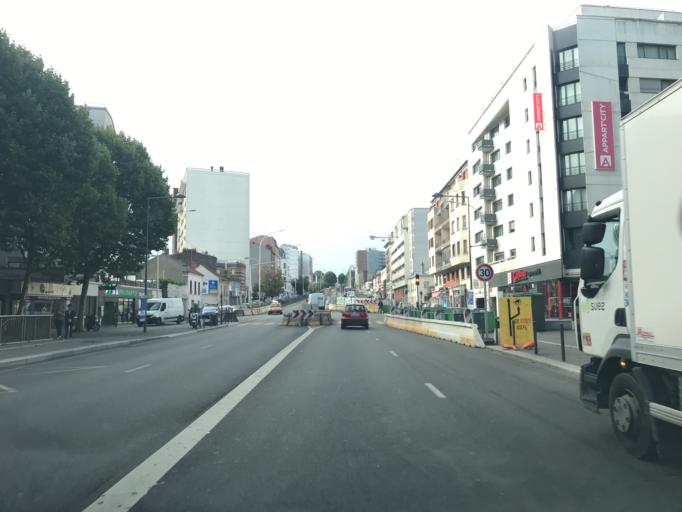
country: FR
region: Ile-de-France
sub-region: Departement du Val-de-Marne
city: Le Kremlin-Bicetre
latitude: 48.8048
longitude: 2.3639
